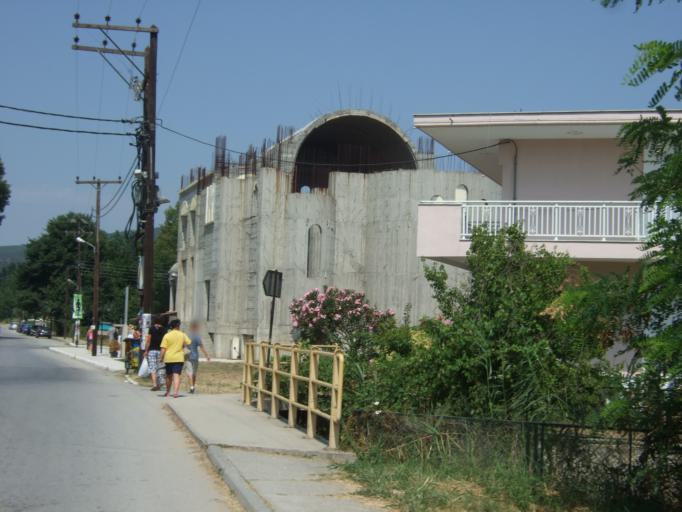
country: GR
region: Central Macedonia
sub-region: Nomos Thessalonikis
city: Stavros
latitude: 40.6664
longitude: 23.6924
